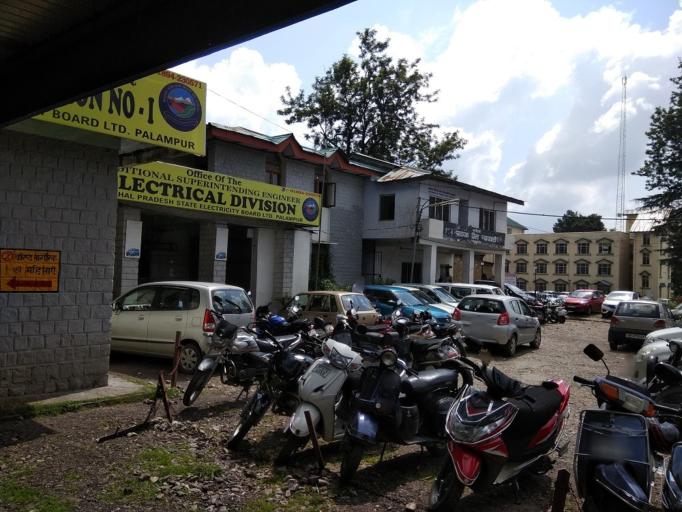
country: IN
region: Himachal Pradesh
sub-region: Kangra
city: Palampur
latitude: 32.1102
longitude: 76.5366
